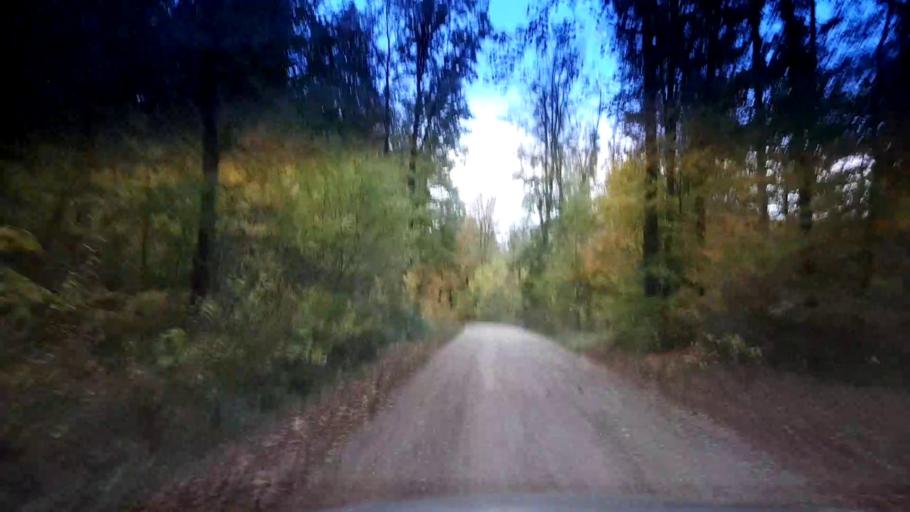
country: DE
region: Bavaria
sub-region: Upper Franconia
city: Schesslitz
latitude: 49.9603
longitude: 11.0314
